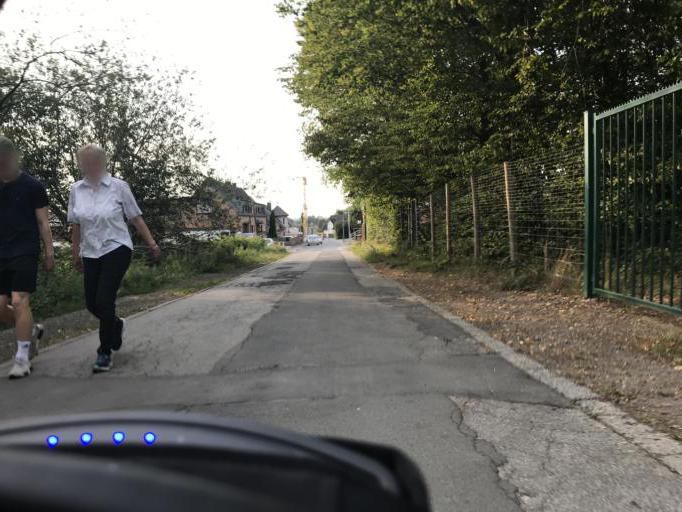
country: DE
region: North Rhine-Westphalia
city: Sankt Augustin
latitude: 50.7711
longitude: 7.2240
